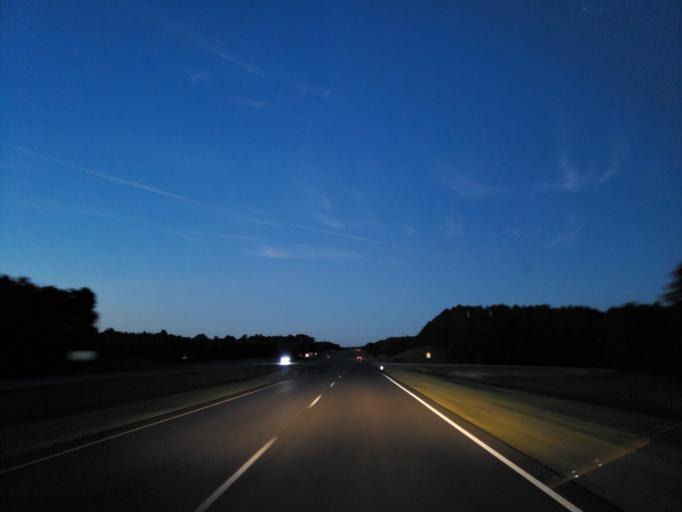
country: US
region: Mississippi
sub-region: Clarke County
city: Quitman
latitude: 32.0113
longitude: -88.6883
